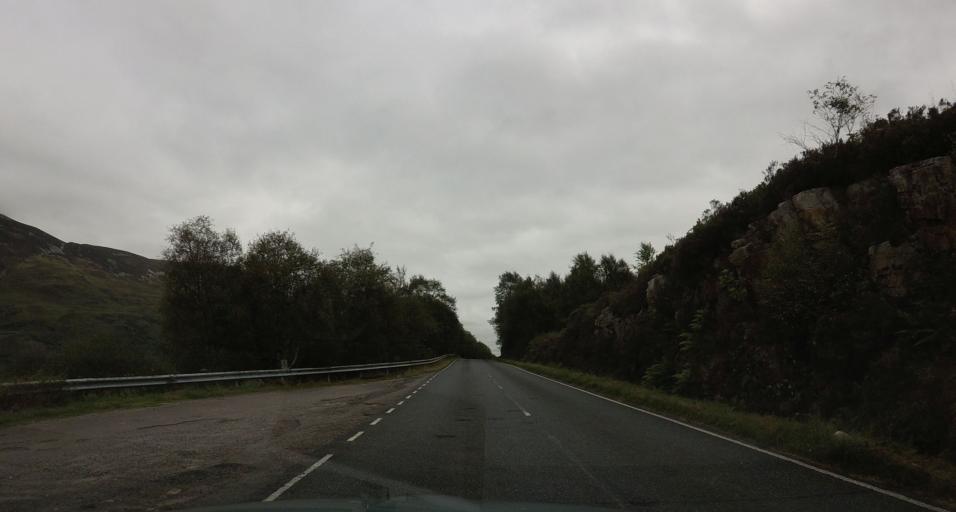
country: GB
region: Scotland
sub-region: Highland
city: Fort William
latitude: 56.6964
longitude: -5.0803
